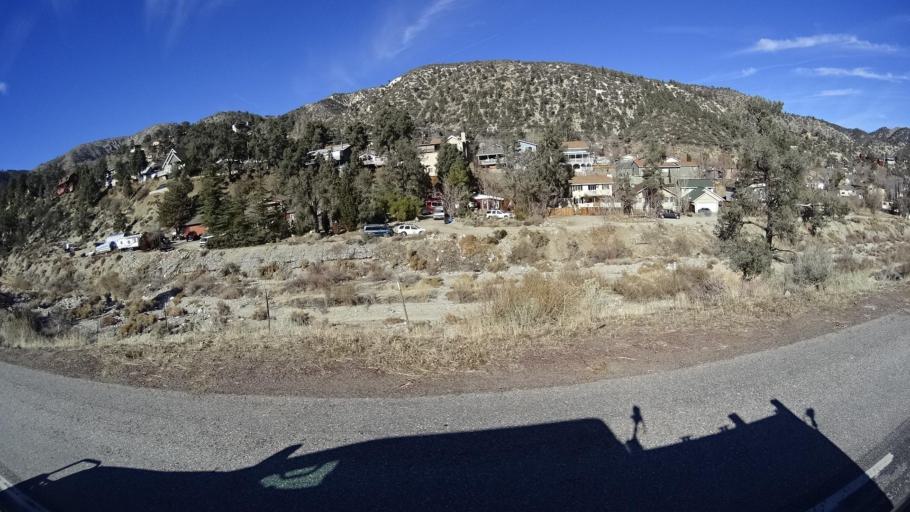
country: US
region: California
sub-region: Kern County
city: Frazier Park
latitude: 34.8210
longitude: -118.9494
